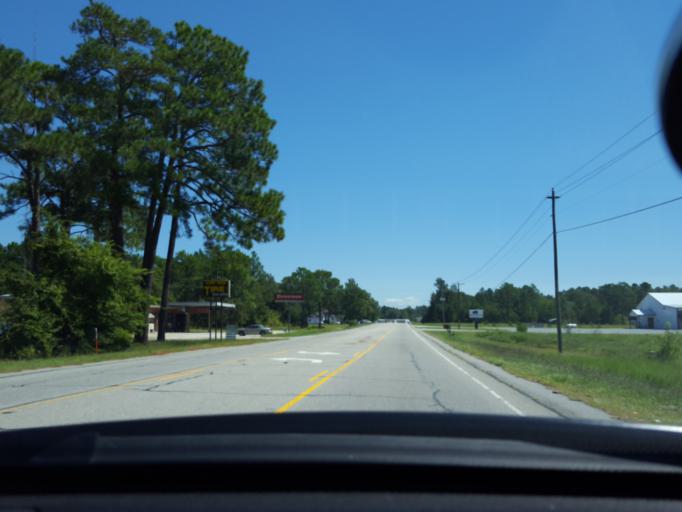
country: US
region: North Carolina
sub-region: Bladen County
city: Elizabethtown
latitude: 34.6480
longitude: -78.5751
